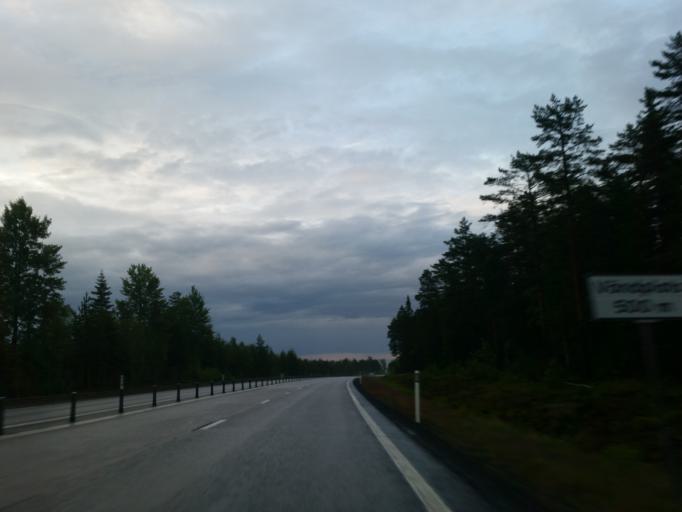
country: SE
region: Vaesterbotten
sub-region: Umea Kommun
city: Saevar
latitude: 63.9523
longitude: 20.6664
